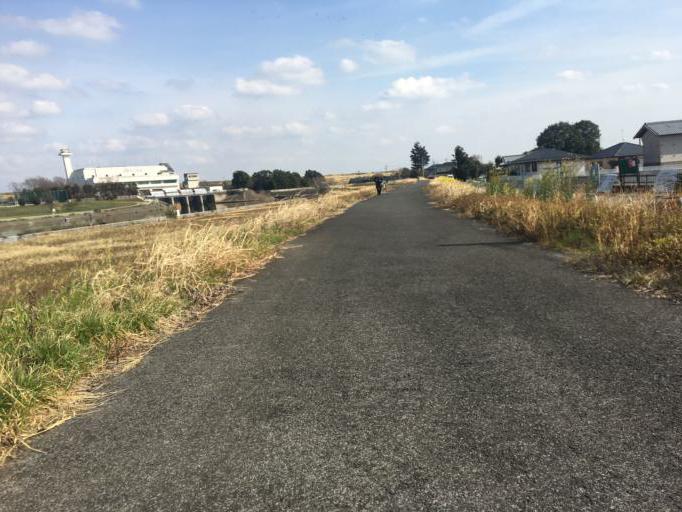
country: JP
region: Saitama
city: Shiki
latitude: 35.8712
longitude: 139.5685
